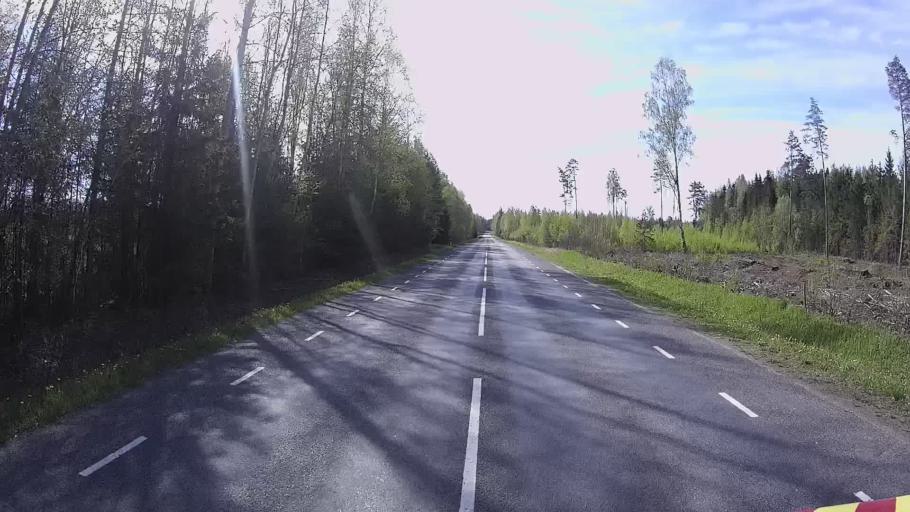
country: EE
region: Polvamaa
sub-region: Polva linn
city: Polva
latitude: 58.1813
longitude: 27.1086
